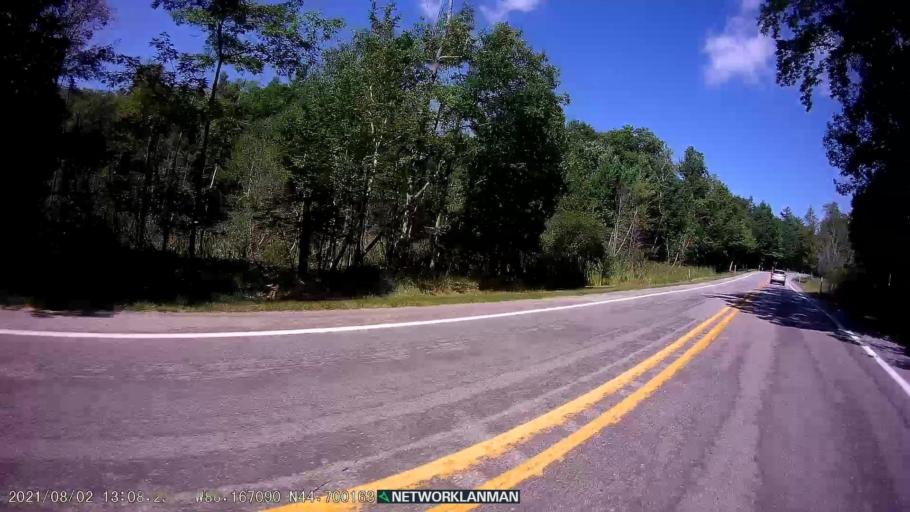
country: US
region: Michigan
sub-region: Benzie County
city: Frankfort
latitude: 44.7003
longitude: -86.1668
